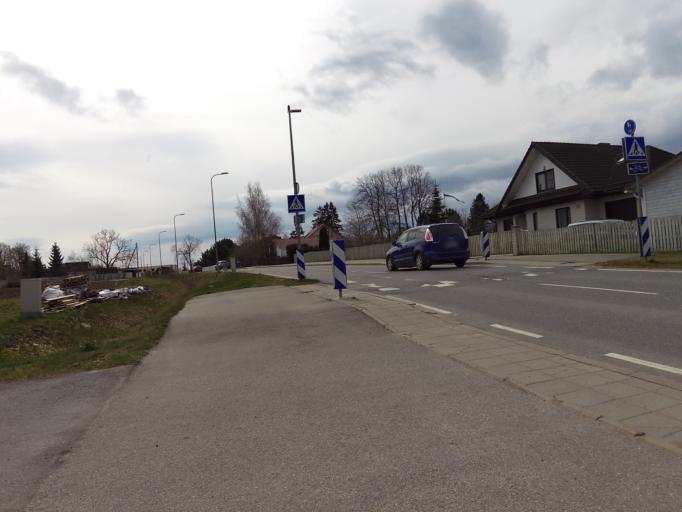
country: EE
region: Harju
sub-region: Rae vald
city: Jueri
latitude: 59.3760
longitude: 24.8420
